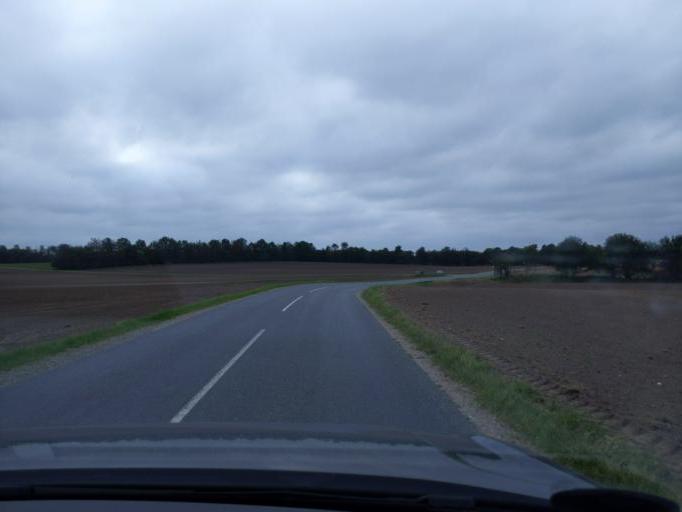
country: DK
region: Central Jutland
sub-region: Viborg Kommune
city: Bjerringbro
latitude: 56.5446
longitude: 9.6325
